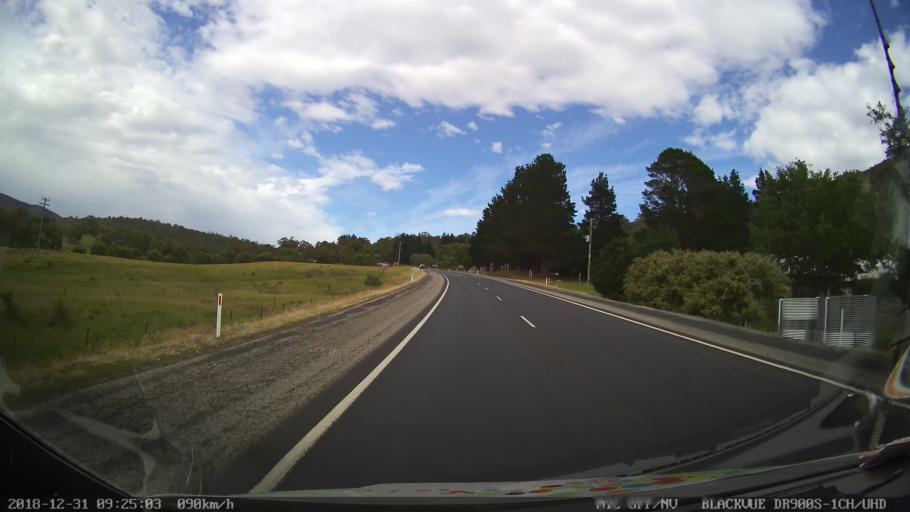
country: AU
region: New South Wales
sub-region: Snowy River
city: Jindabyne
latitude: -36.4411
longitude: 148.5123
